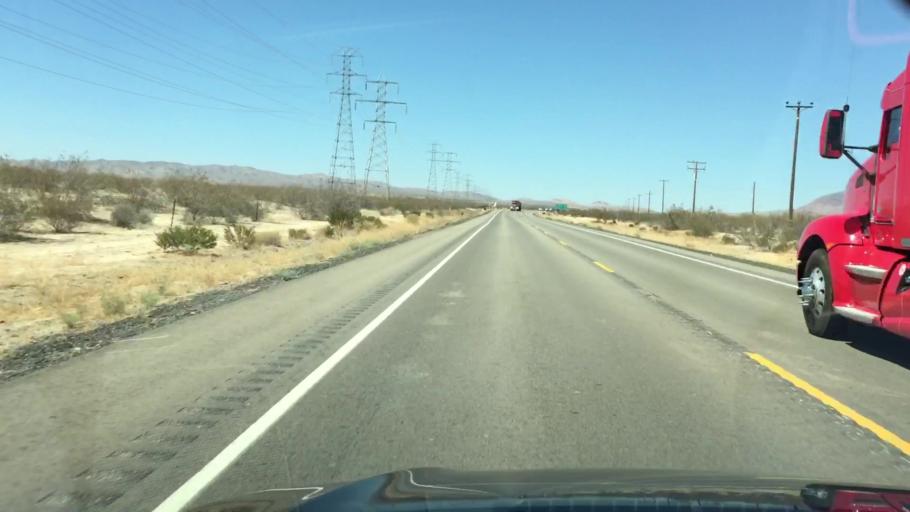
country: US
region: California
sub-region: Kern County
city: Boron
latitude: 35.2319
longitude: -117.6085
